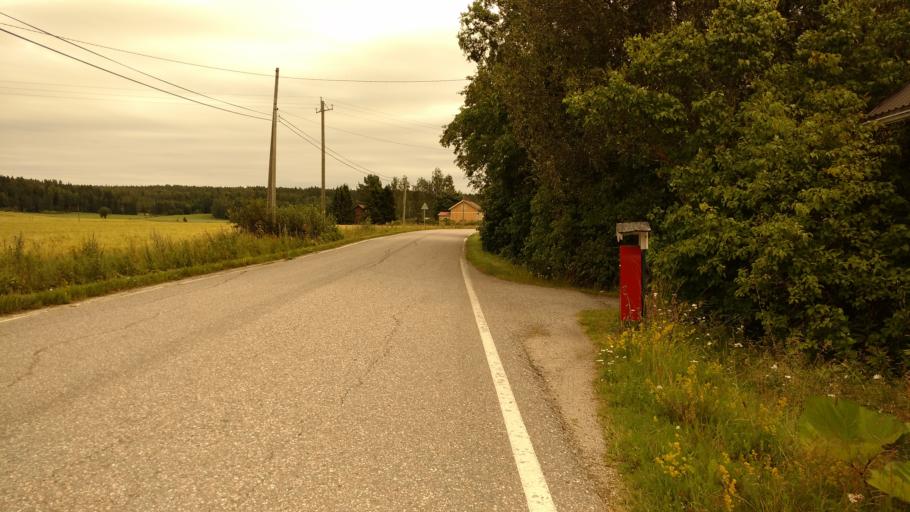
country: FI
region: Varsinais-Suomi
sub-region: Loimaa
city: Marttila
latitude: 60.4170
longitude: 22.8551
